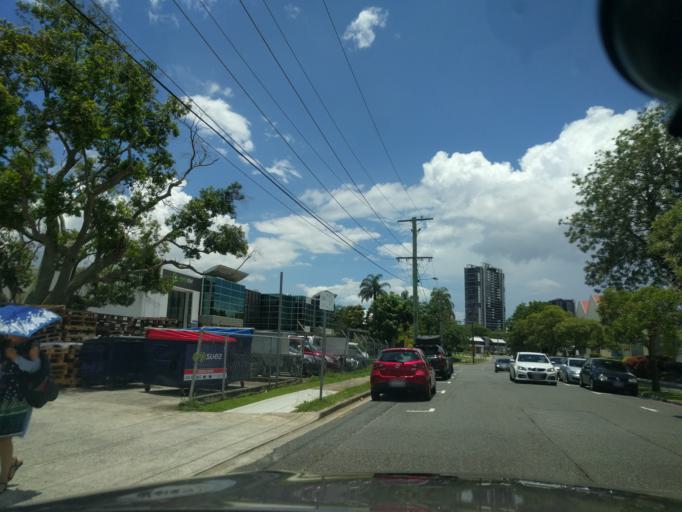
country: AU
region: Queensland
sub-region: Brisbane
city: Milton
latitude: -27.4735
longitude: 153.0008
